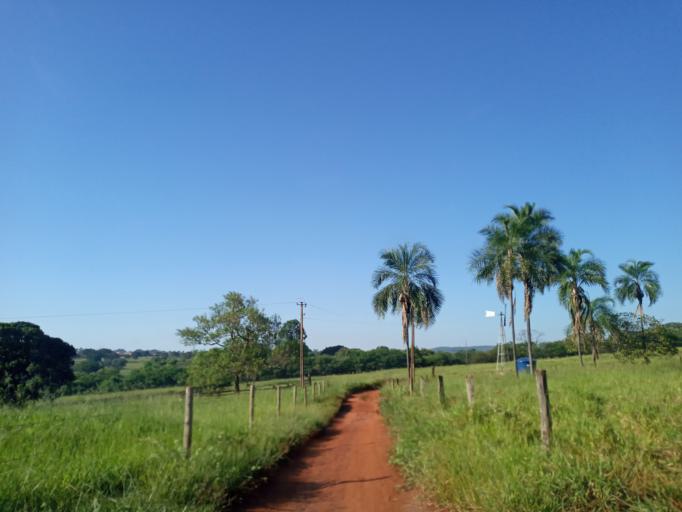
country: BR
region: Minas Gerais
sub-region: Ituiutaba
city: Ituiutaba
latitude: -18.9761
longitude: -49.4960
